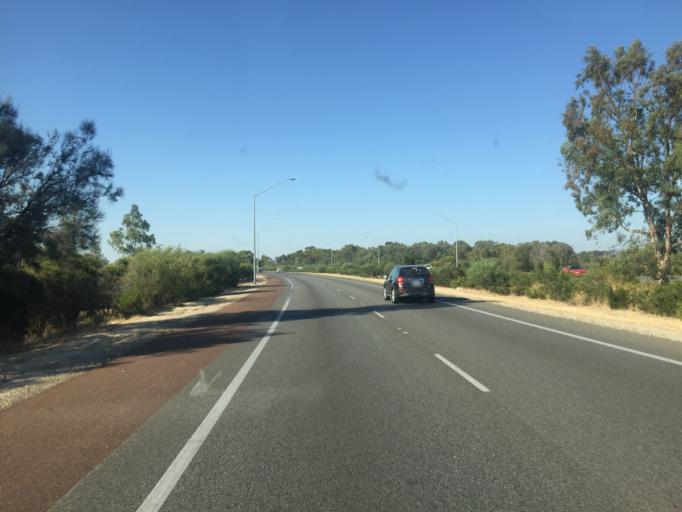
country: AU
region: Western Australia
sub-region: Gosnells
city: Kenwick
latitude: -32.0256
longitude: 115.9713
